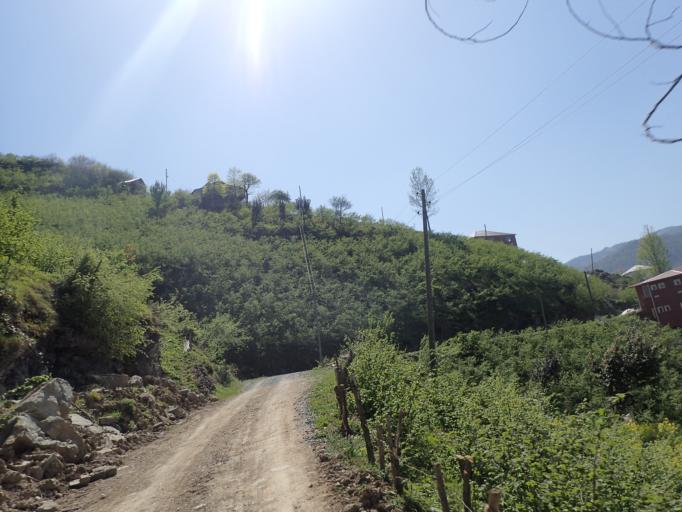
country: TR
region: Ordu
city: Kabaduz
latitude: 40.7422
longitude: 37.8738
